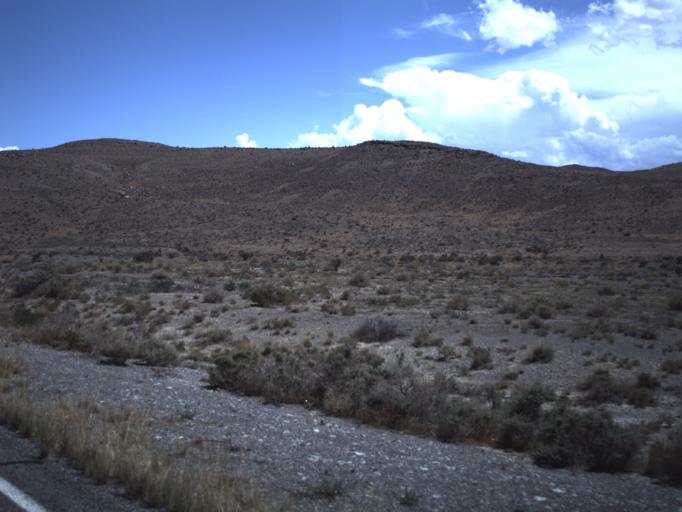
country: US
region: Utah
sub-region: Beaver County
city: Milford
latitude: 39.0240
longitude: -113.3595
